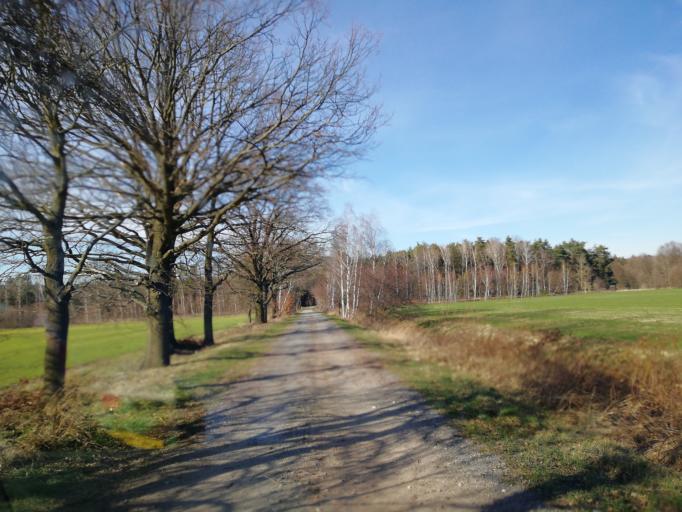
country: DE
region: Brandenburg
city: Ruckersdorf
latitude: 51.5602
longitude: 13.5916
